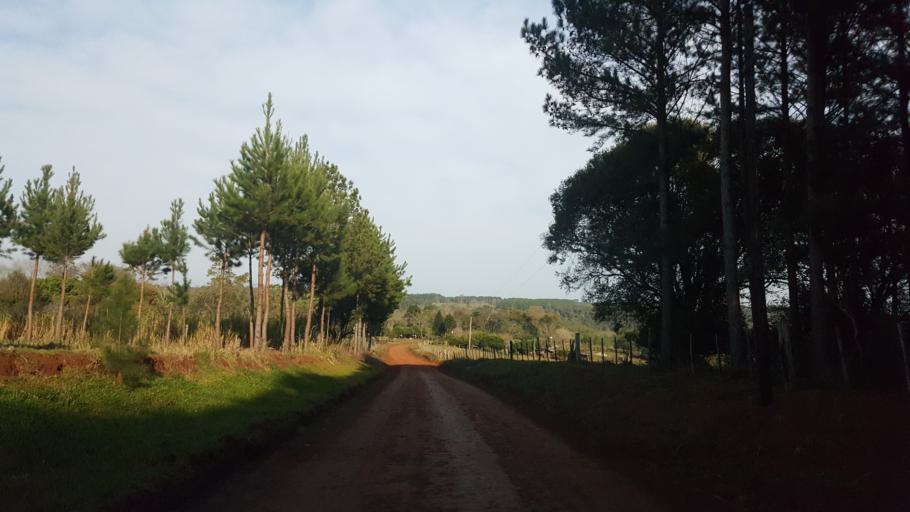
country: AR
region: Misiones
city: Capiovi
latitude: -26.9150
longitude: -55.0758
